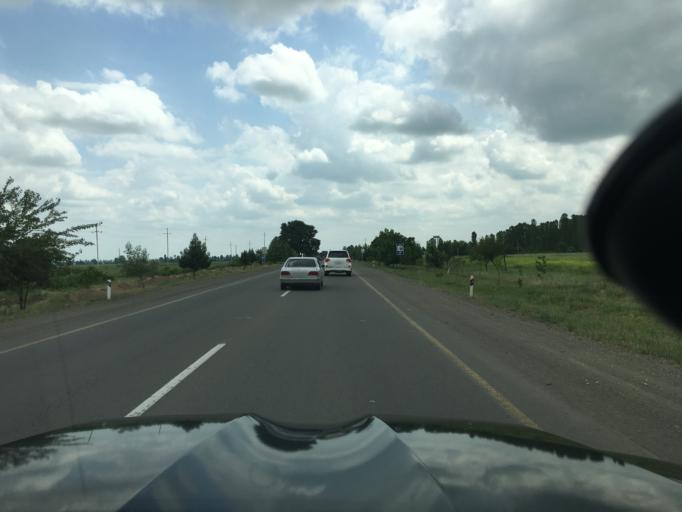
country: AZ
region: Tovuz
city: Tovuz
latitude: 40.9635
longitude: 45.7118
